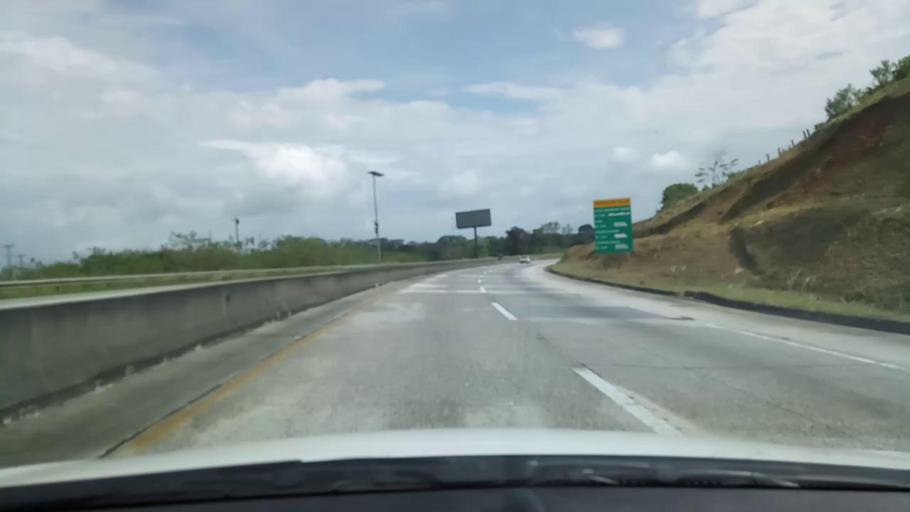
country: PA
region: Colon
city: Buena Vista
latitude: 9.2718
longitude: -79.7088
